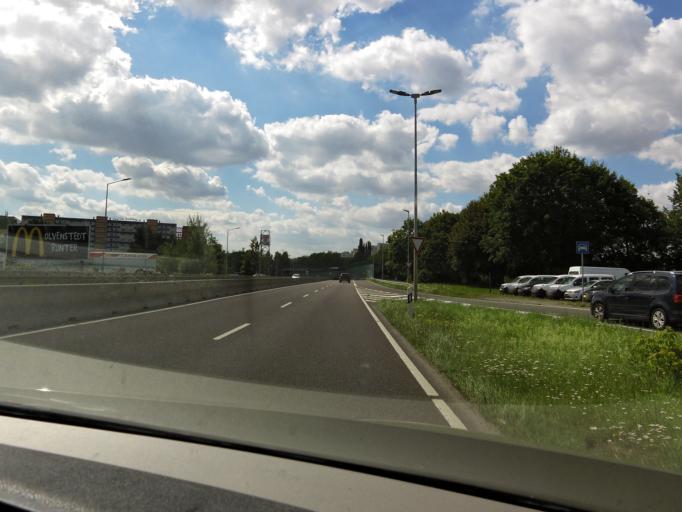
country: DE
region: Saxony-Anhalt
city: Neue Neustadt
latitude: 52.1754
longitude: 11.6280
